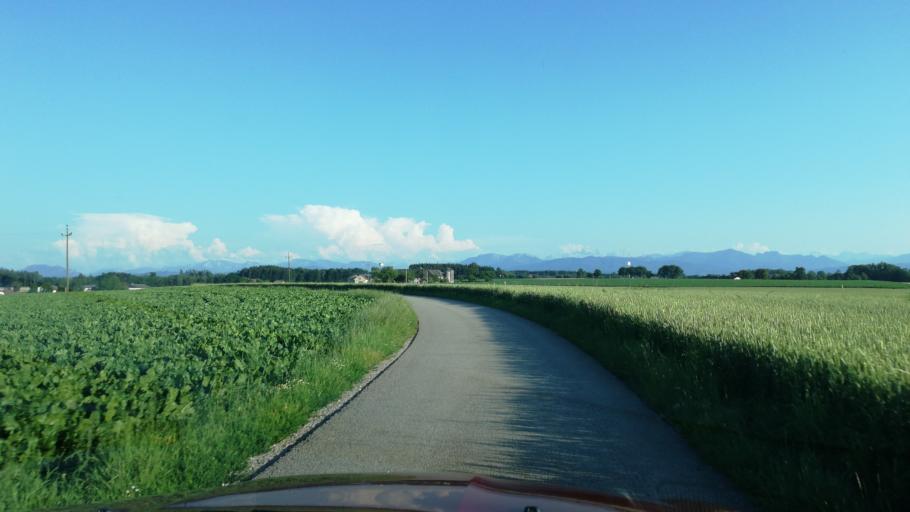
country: AT
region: Upper Austria
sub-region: Wels-Land
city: Sattledt
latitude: 48.0781
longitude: 14.0327
